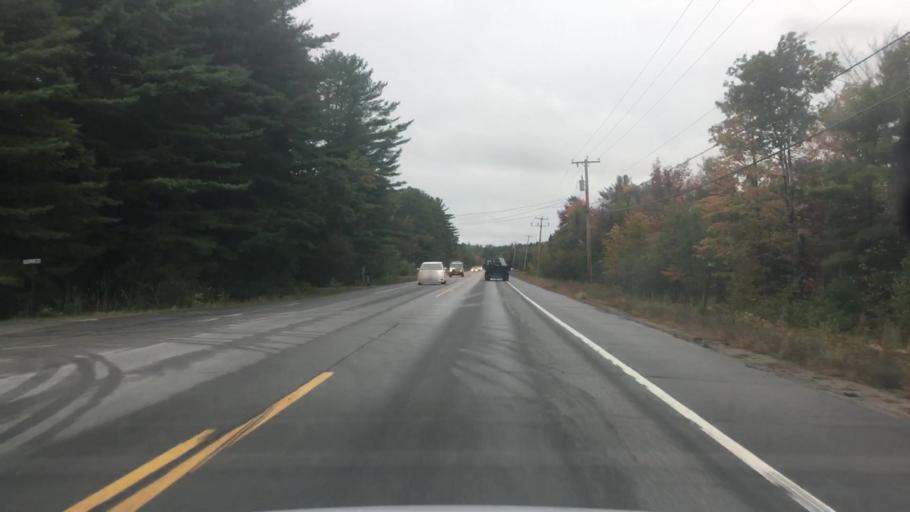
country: US
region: Maine
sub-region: Kennebec County
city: Belgrade
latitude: 44.4268
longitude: -69.8307
